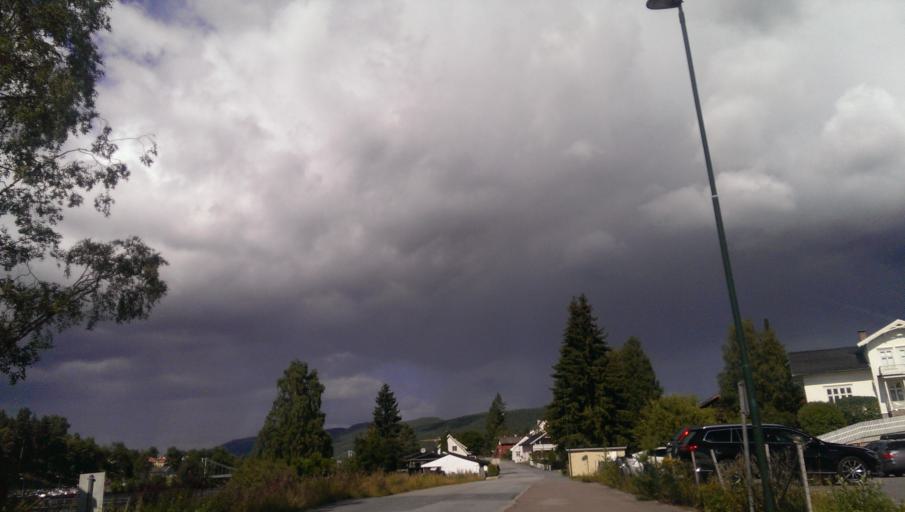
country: NO
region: Buskerud
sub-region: Kongsberg
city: Kongsberg
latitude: 59.6581
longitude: 9.6533
